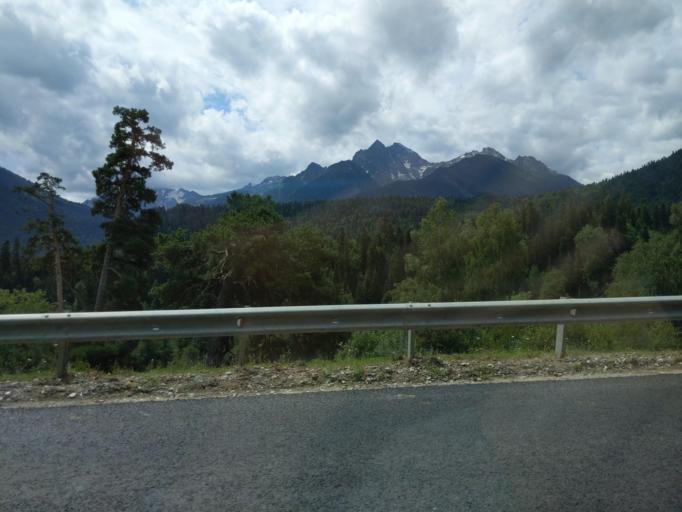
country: RU
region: Karachayevo-Cherkesiya
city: Nizhniy Arkhyz
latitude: 43.5371
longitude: 41.2223
